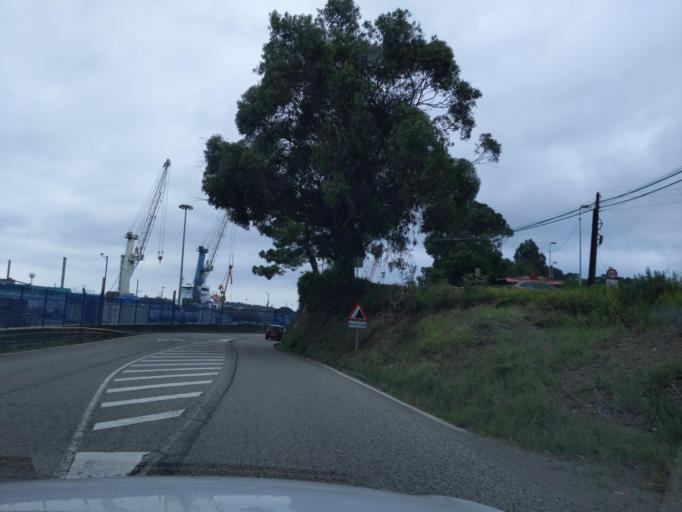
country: ES
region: Asturias
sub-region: Province of Asturias
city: Aviles
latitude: 43.5748
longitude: -5.9174
